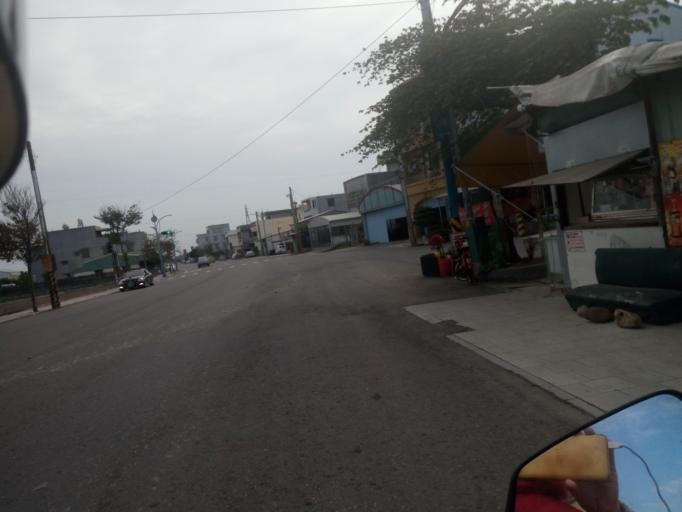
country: TW
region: Taiwan
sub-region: Chiayi
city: Taibao
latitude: 23.4853
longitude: 120.3353
